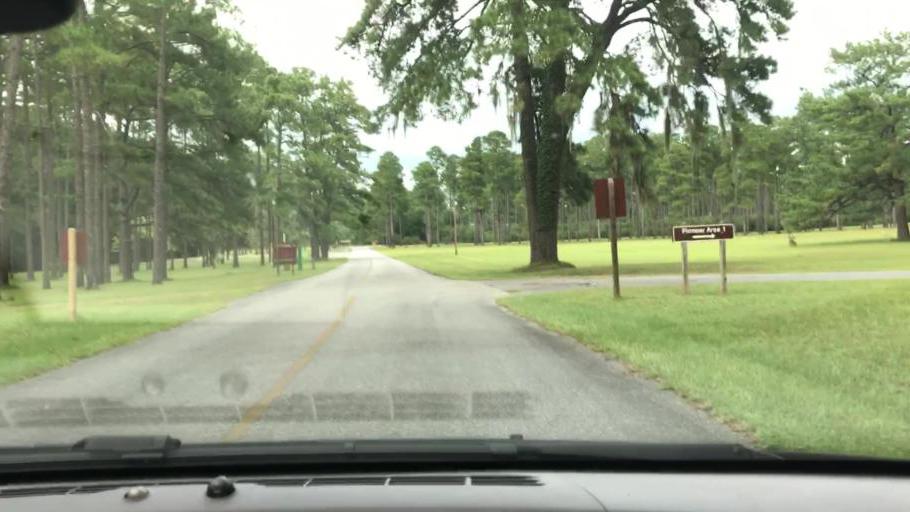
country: US
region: Georgia
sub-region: Early County
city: Blakely
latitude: 31.4687
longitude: -84.9272
